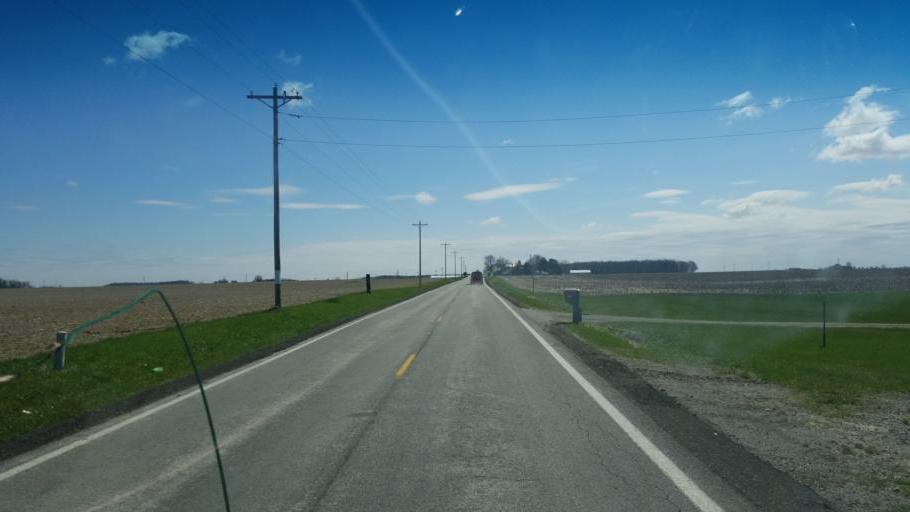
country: US
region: Ohio
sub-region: Crawford County
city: Crestline
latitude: 40.8644
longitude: -82.7506
